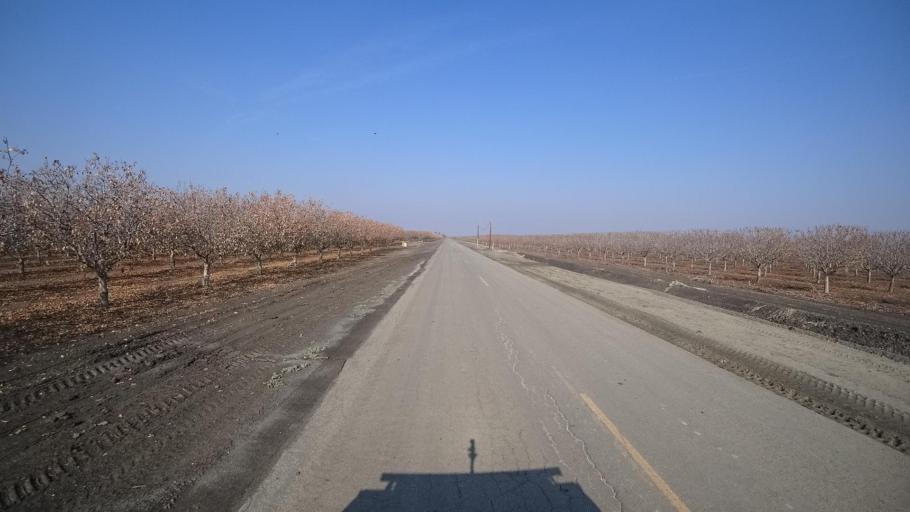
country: US
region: California
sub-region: Kern County
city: Buttonwillow
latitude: 35.3498
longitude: -119.4293
